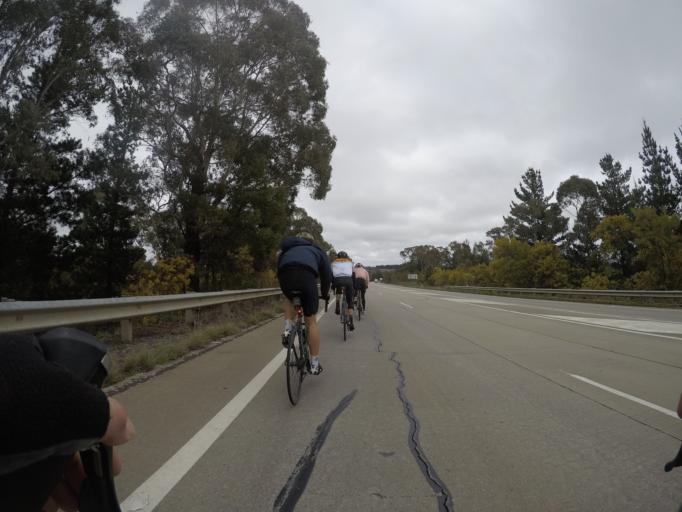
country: AU
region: New South Wales
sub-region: Lithgow
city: Lithgow
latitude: -33.4451
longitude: 150.0504
